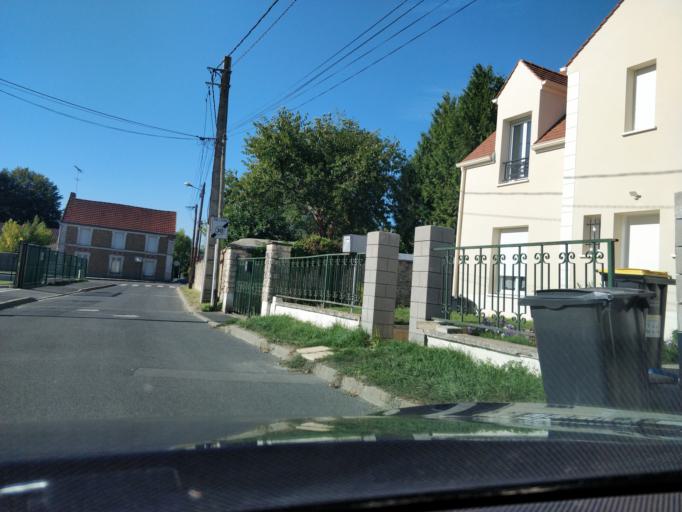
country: FR
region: Ile-de-France
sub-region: Departement de l'Essonne
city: Forges-les-Bains
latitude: 48.6299
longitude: 2.0942
